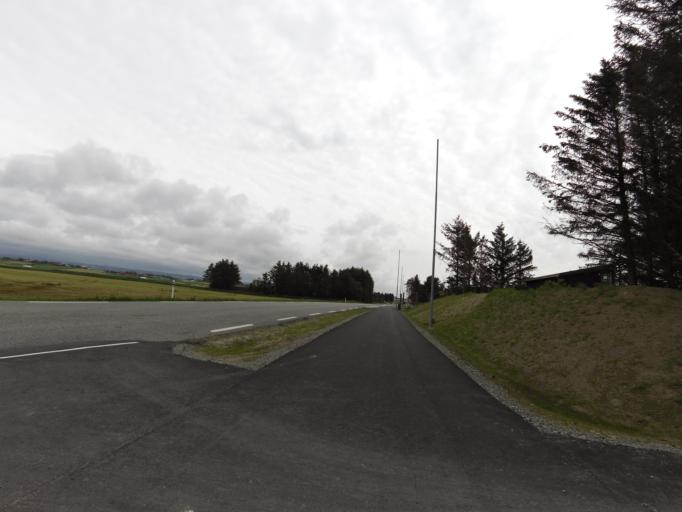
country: NO
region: Rogaland
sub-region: Ha
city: Naerbo
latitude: 58.6910
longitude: 5.5579
